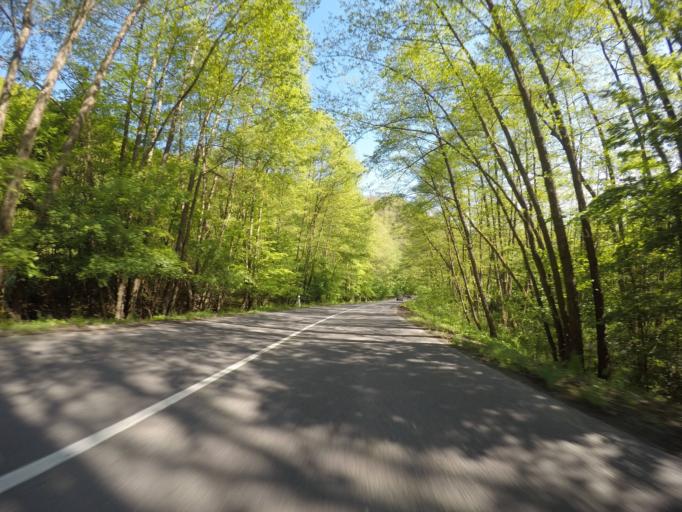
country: SK
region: Banskobystricky
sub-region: Okres Banska Bystrica
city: Banska Stiavnica
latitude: 48.5580
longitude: 19.0030
